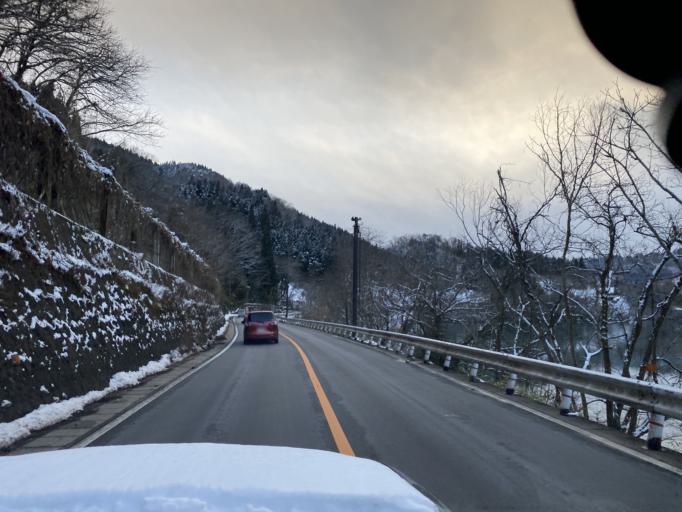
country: JP
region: Nagano
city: Nagano-shi
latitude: 36.6019
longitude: 138.0573
